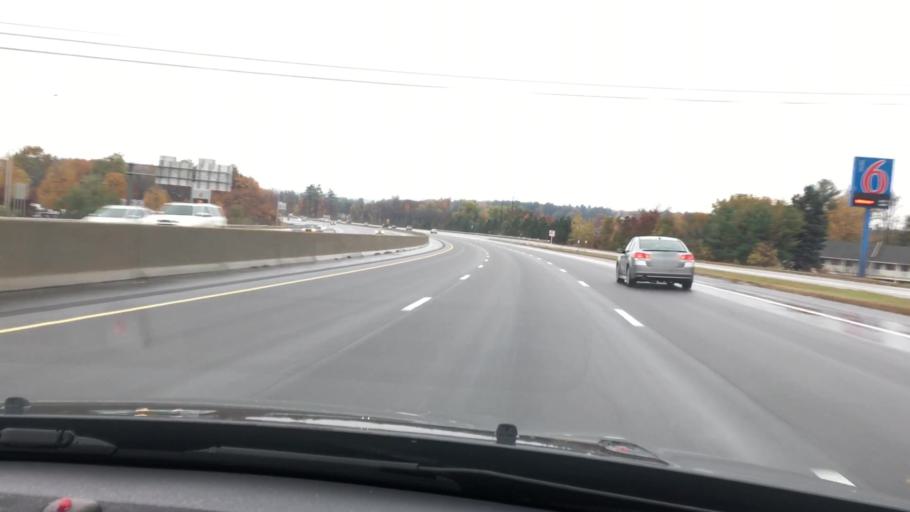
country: US
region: New Hampshire
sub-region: Hillsborough County
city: Nashua
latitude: 42.7446
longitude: -71.4916
